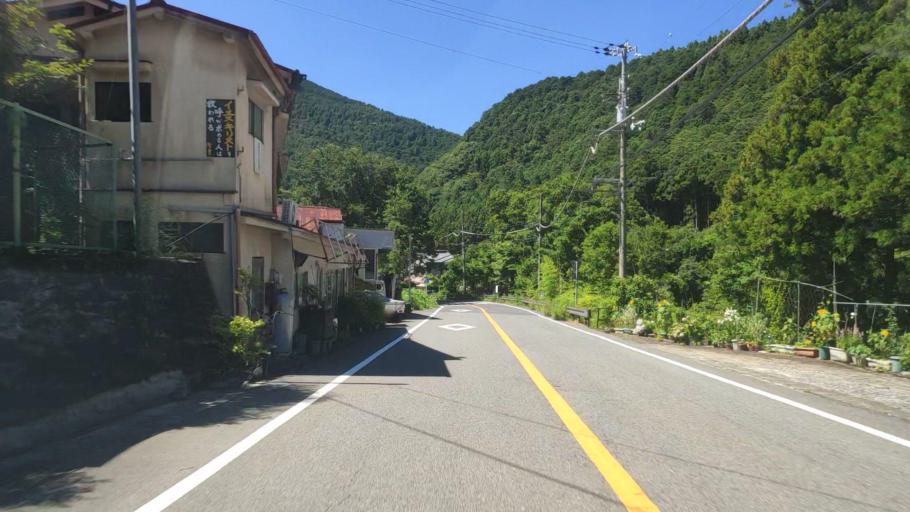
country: JP
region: Nara
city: Yoshino-cho
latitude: 34.2875
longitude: 136.0026
